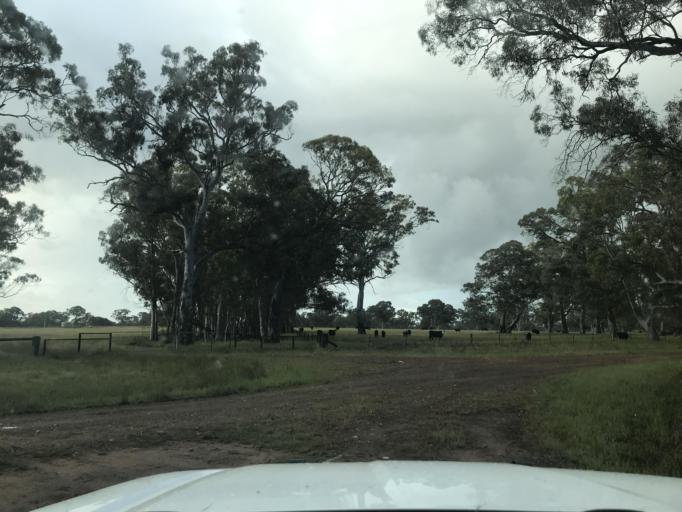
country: AU
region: South Australia
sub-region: Wattle Range
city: Penola
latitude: -37.1750
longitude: 141.3281
